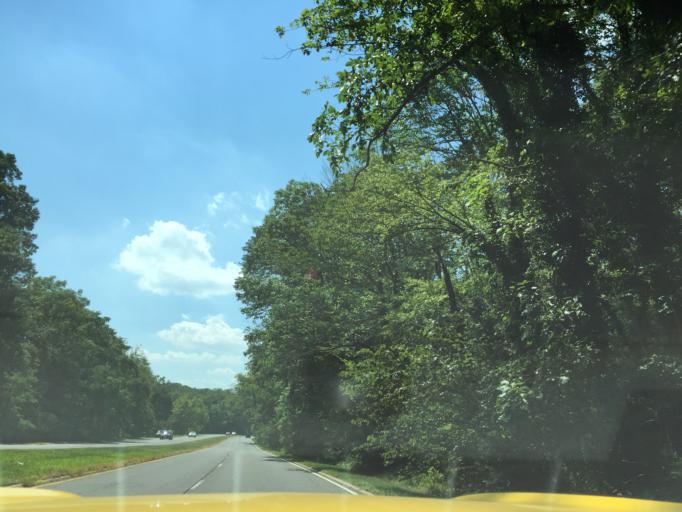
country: US
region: Maryland
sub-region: Montgomery County
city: Cabin John
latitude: 38.9731
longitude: -77.1661
